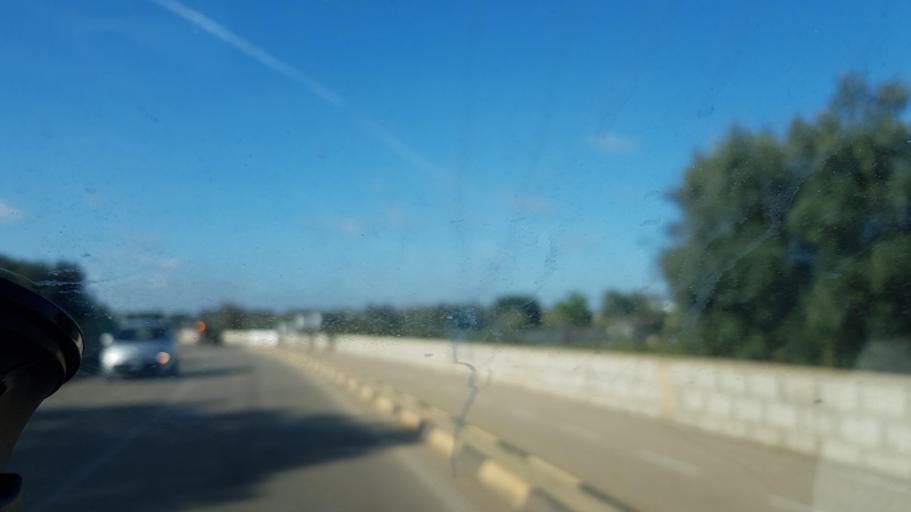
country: IT
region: Apulia
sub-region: Provincia di Brindisi
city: San Vito dei Normanni
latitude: 40.6647
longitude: 17.7130
